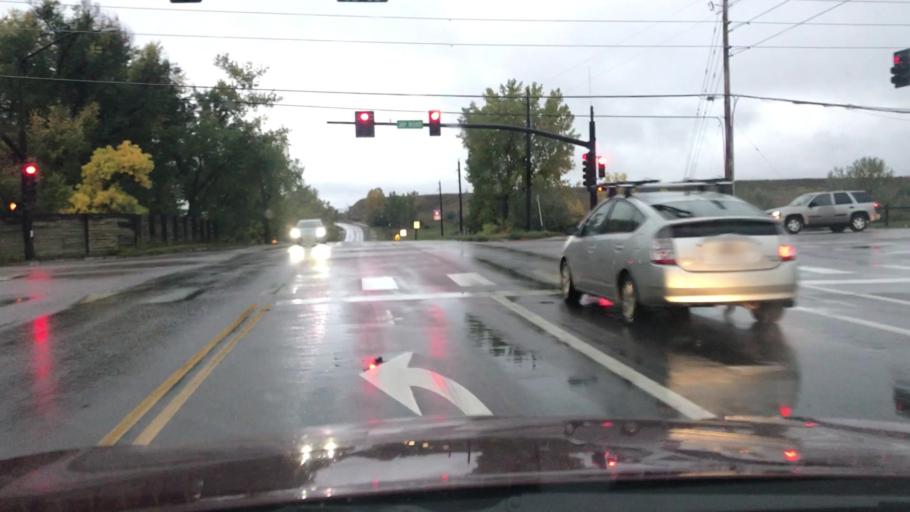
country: US
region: Colorado
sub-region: Boulder County
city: Gunbarrel
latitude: 40.0512
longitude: -105.2069
